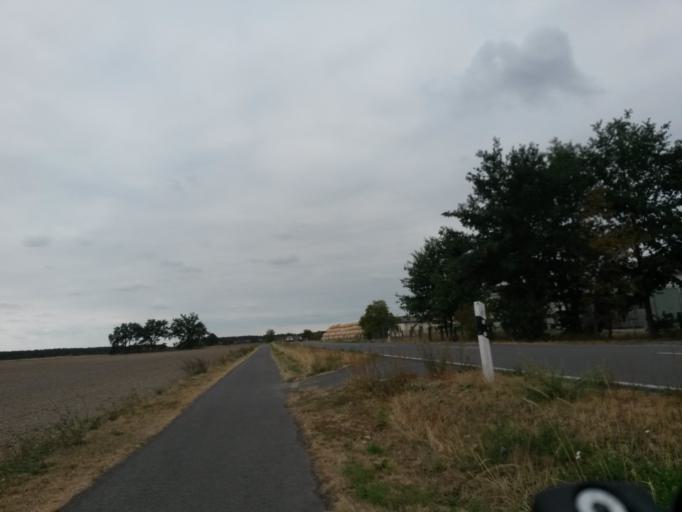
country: DE
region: Saxony-Anhalt
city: Muhlanger
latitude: 51.8659
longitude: 12.7836
